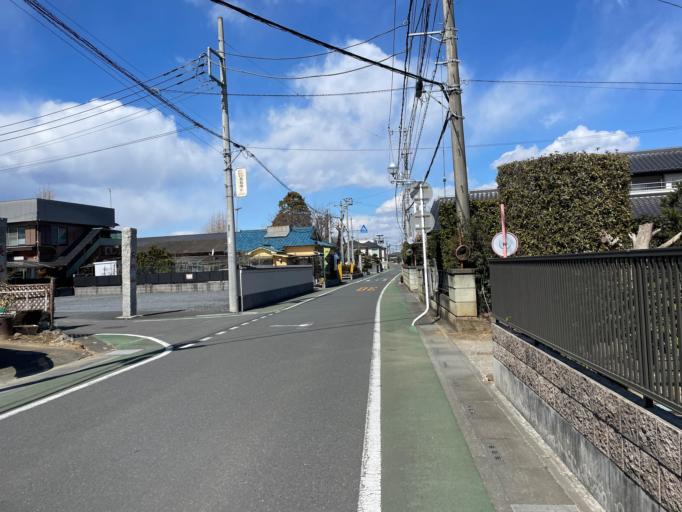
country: JP
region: Saitama
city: Sakado
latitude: 35.9993
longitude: 139.4028
